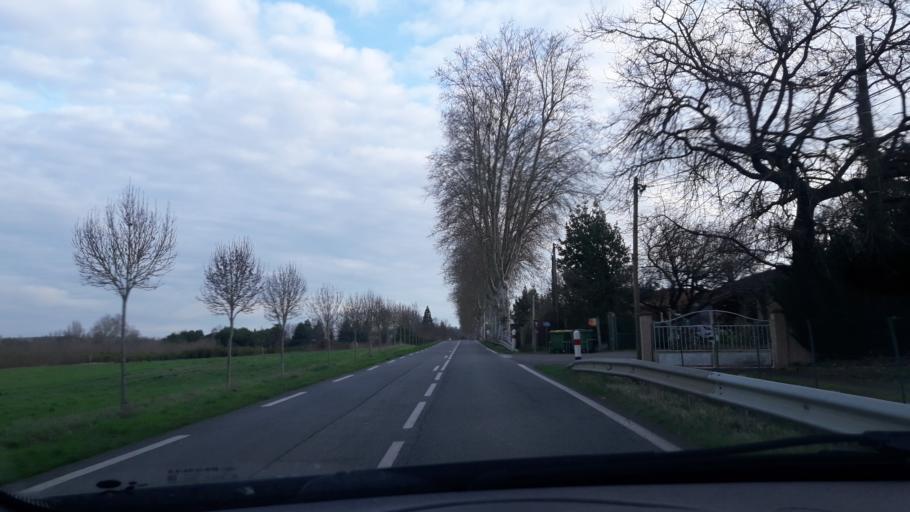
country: FR
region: Midi-Pyrenees
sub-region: Departement de la Haute-Garonne
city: Montaigut-sur-Save
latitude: 43.6978
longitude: 1.2372
